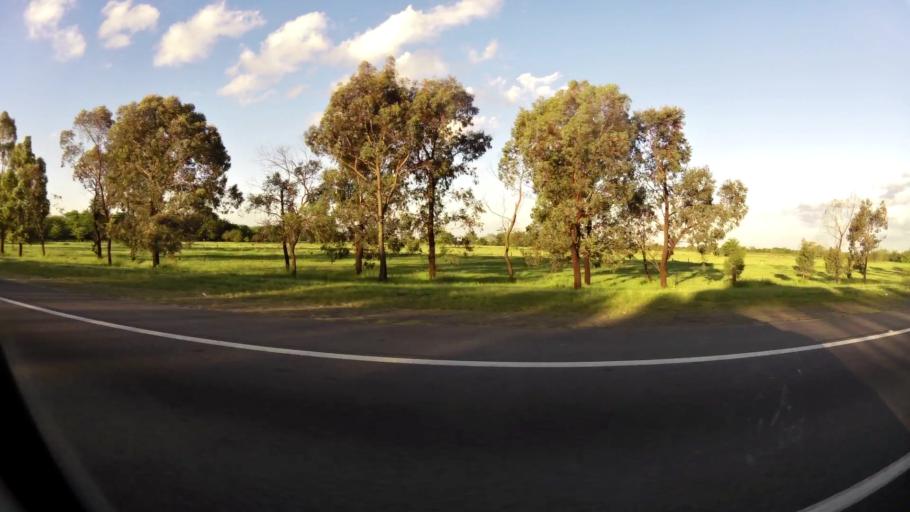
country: AR
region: Buenos Aires
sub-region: Partido de Quilmes
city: Quilmes
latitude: -34.8167
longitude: -58.1087
